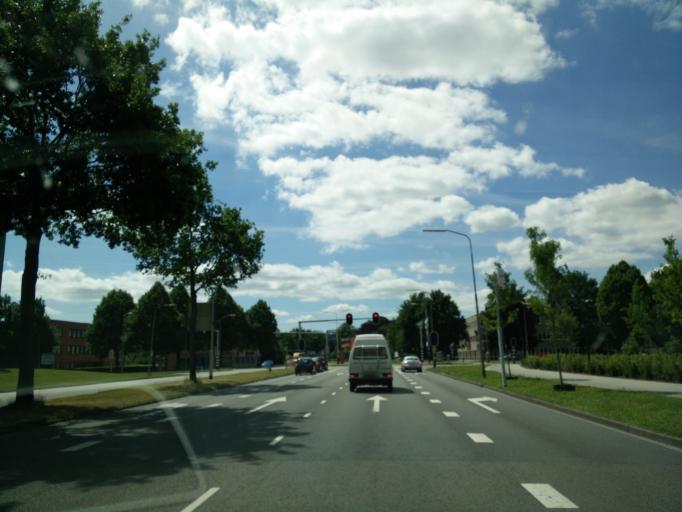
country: NL
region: Drenthe
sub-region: Gemeente Emmen
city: Emmen
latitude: 52.7780
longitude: 6.8921
